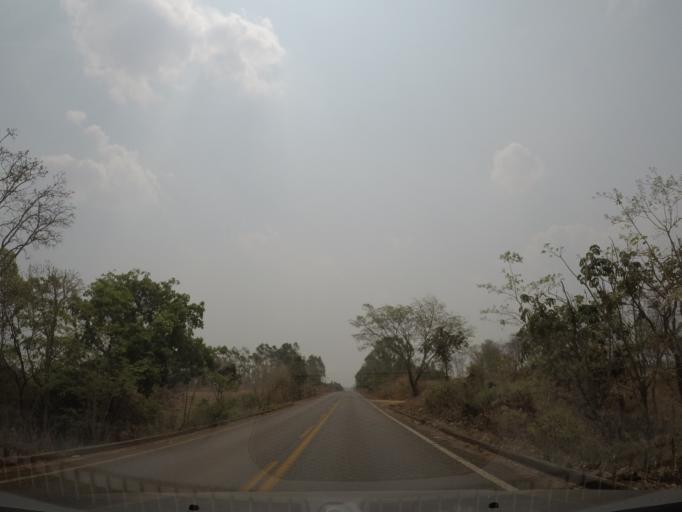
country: BR
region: Goias
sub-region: Pirenopolis
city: Pirenopolis
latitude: -15.9111
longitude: -48.8607
